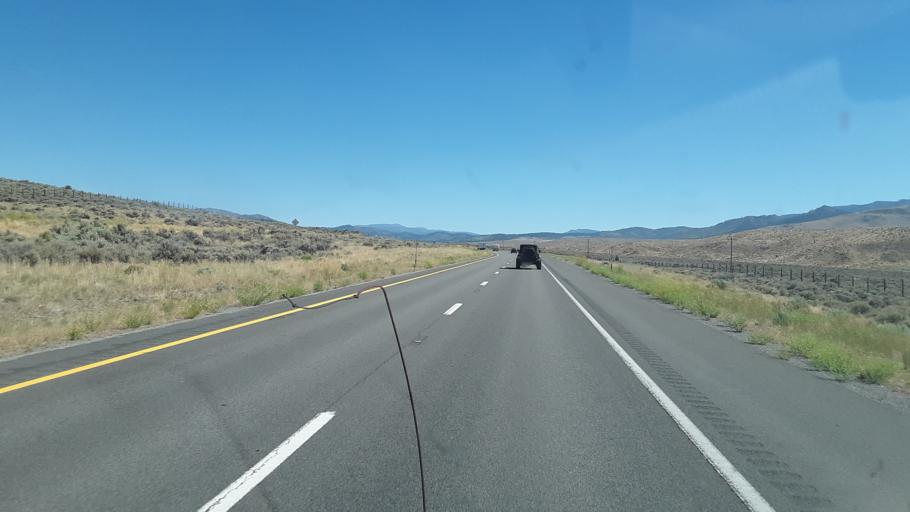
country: US
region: Nevada
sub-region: Washoe County
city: Cold Springs
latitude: 39.7205
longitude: -120.0383
